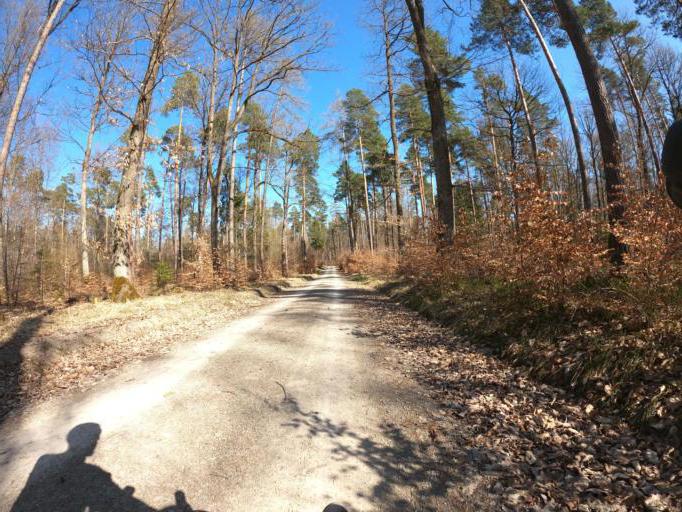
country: DE
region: Baden-Wuerttemberg
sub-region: Tuebingen Region
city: Rangendingen
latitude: 48.3943
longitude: 8.9130
